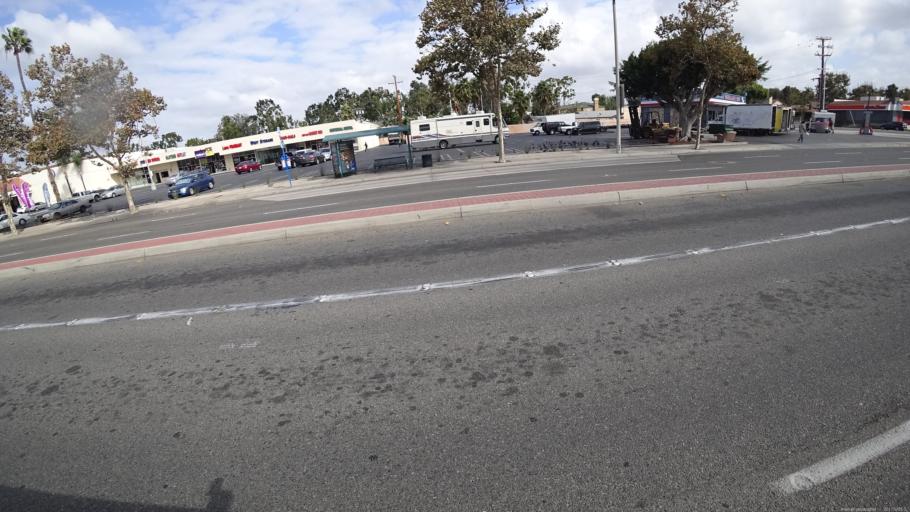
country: US
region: California
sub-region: Orange County
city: Santa Ana
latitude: 33.7598
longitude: -117.9037
